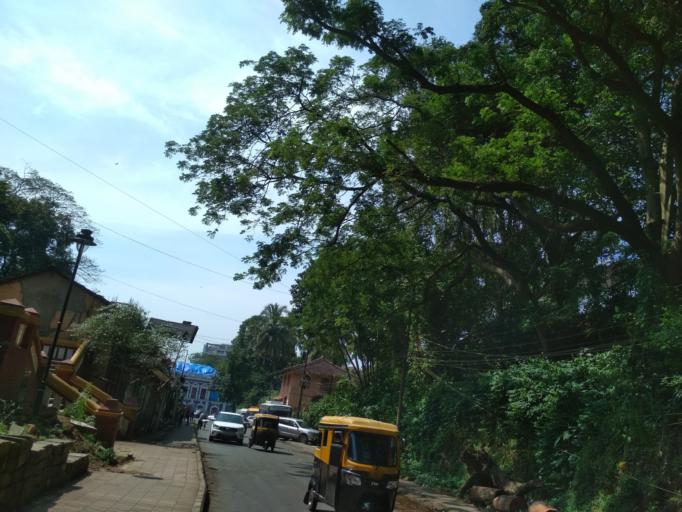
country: IN
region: Goa
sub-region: North Goa
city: Panaji
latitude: 15.4980
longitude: 73.8301
